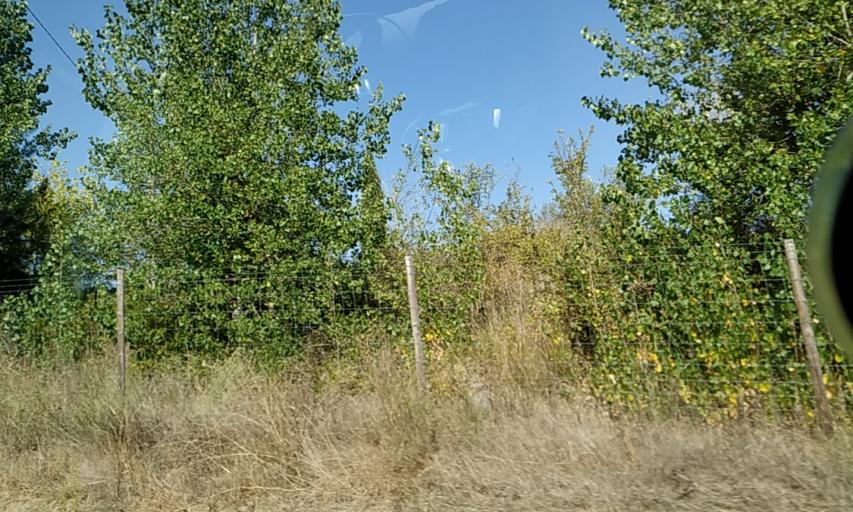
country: PT
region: Santarem
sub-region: Coruche
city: Coruche
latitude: 38.8019
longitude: -8.5789
